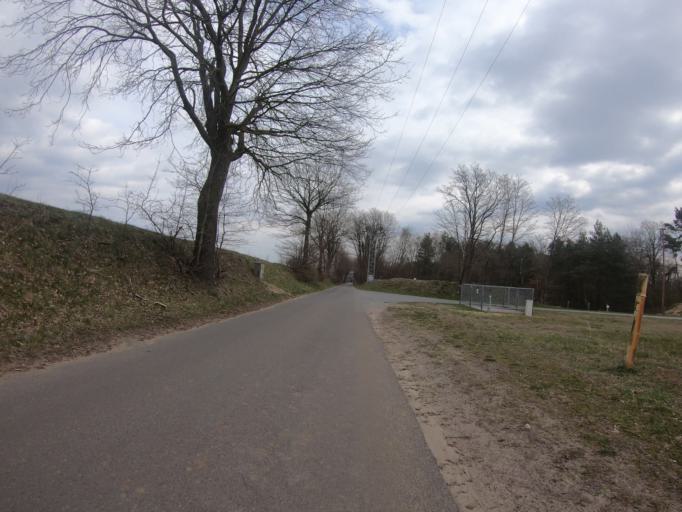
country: DE
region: Lower Saxony
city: Hankensbuttel
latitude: 52.7148
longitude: 10.6109
